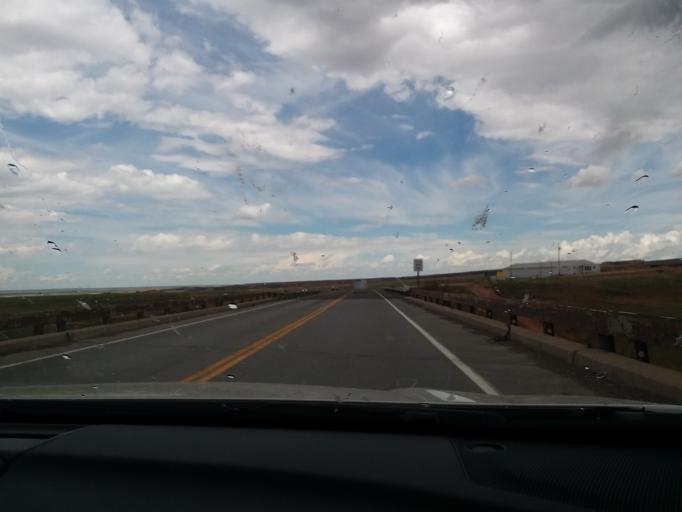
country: US
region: Wyoming
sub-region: Albany County
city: Laramie
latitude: 41.1308
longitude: -105.5515
